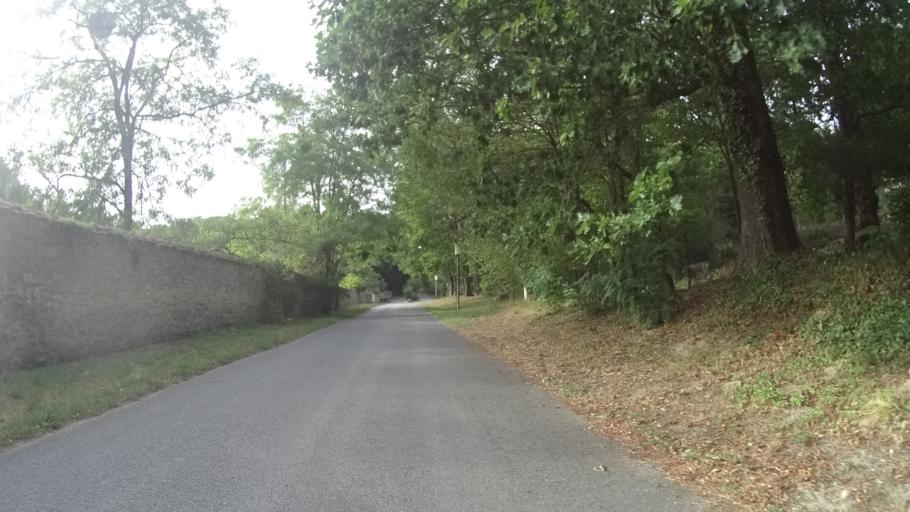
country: FR
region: Picardie
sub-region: Departement de l'Oise
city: Ver-sur-Launette
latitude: 49.1296
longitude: 2.7017
